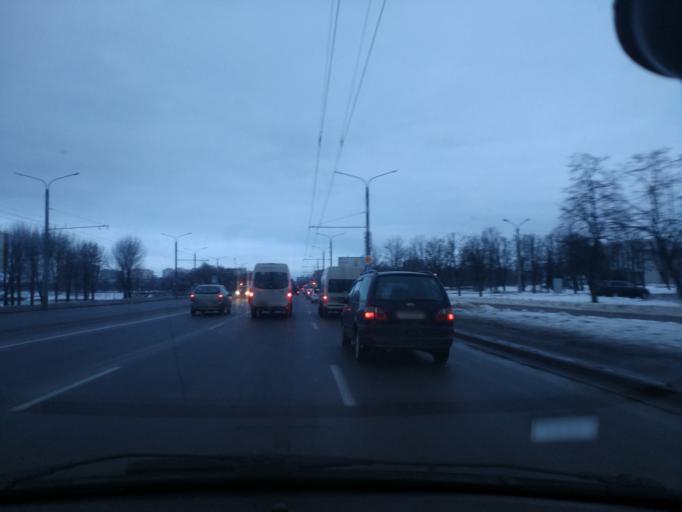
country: BY
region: Mogilev
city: Mahilyow
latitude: 53.8884
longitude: 30.3305
